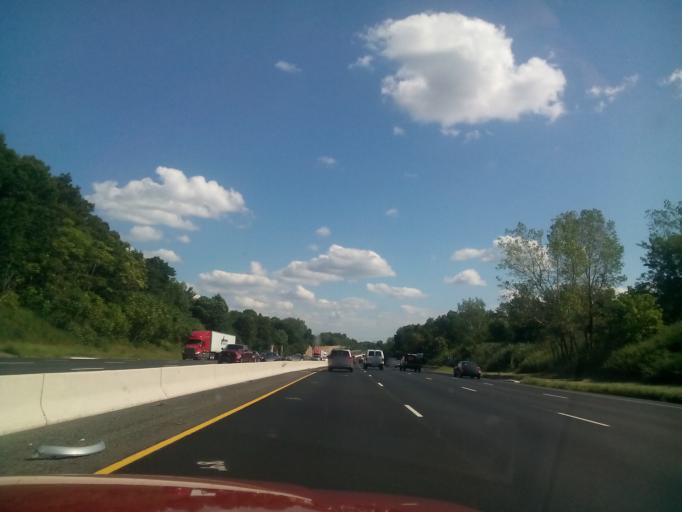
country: US
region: New Jersey
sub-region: Morris County
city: Rockaway
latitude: 40.9028
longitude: -74.4933
